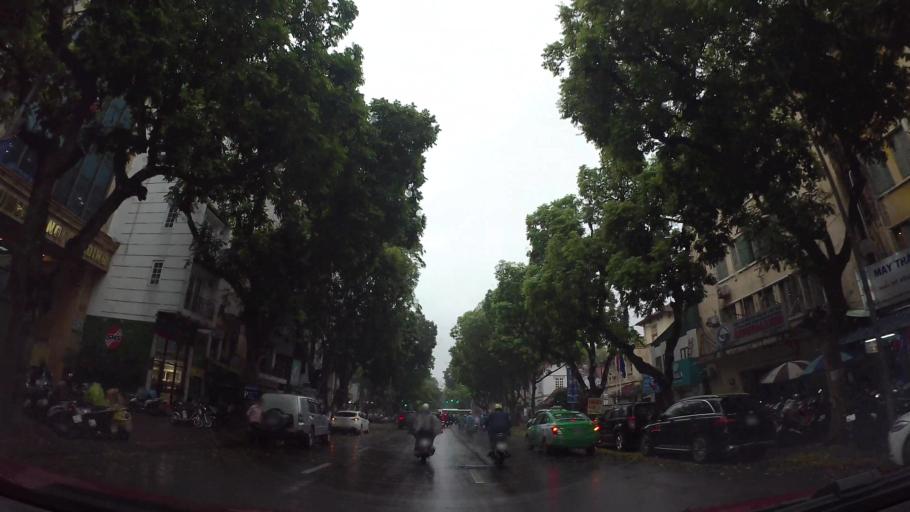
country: VN
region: Ha Noi
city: Hoan Kiem
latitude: 21.0216
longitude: 105.8540
